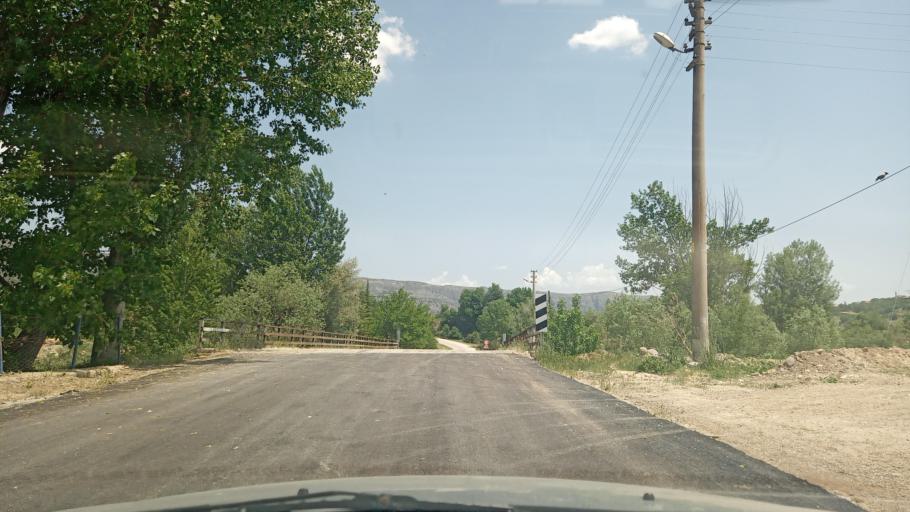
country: TR
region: Bolu
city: Seben
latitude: 40.4074
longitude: 31.5789
